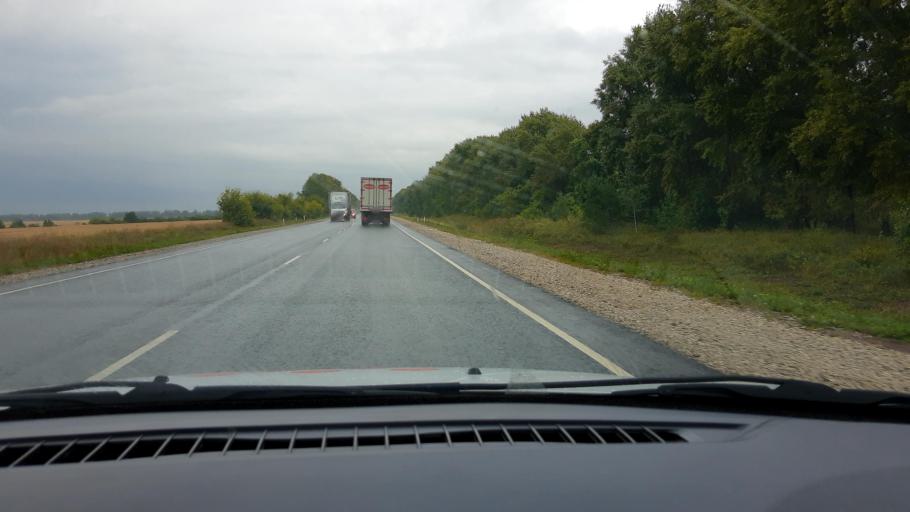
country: RU
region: Chuvashia
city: Yantikovo
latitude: 55.7896
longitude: 47.7036
